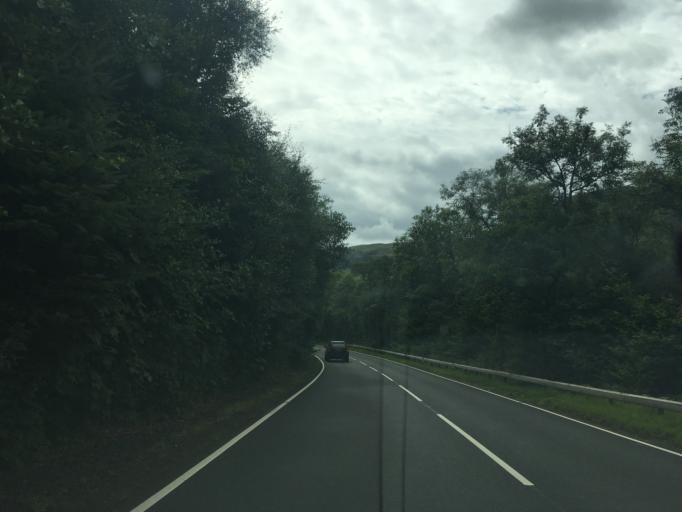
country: GB
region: Scotland
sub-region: Stirling
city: Callander
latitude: 56.2699
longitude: -4.2838
